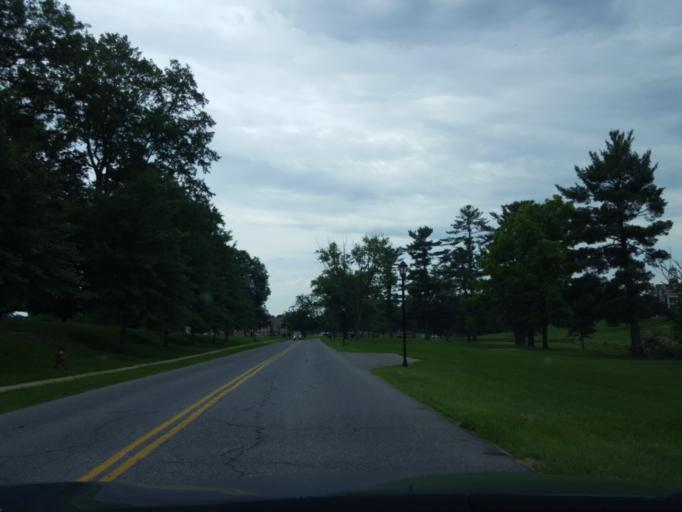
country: US
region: Maryland
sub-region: Carroll County
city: Sykesville
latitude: 39.3859
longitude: -76.9597
